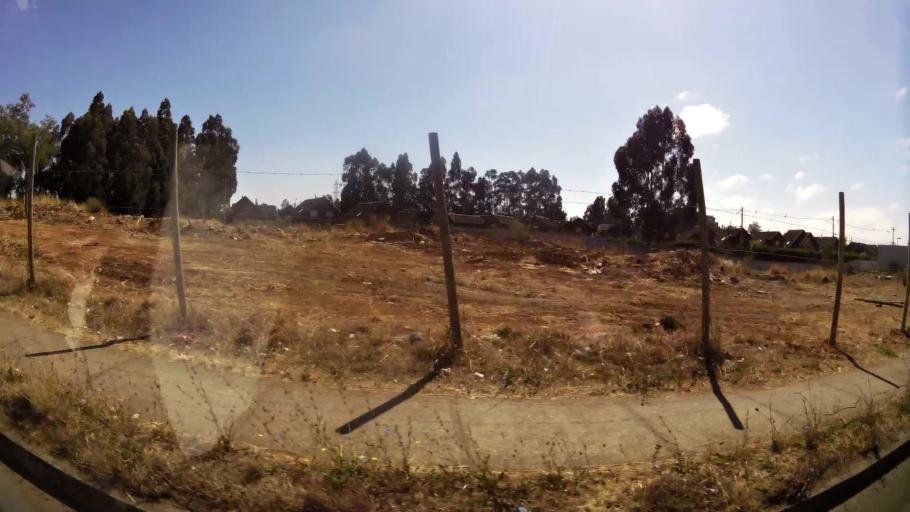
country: CL
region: Biobio
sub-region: Provincia de Concepcion
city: Concepcion
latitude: -36.7854
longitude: -73.0546
